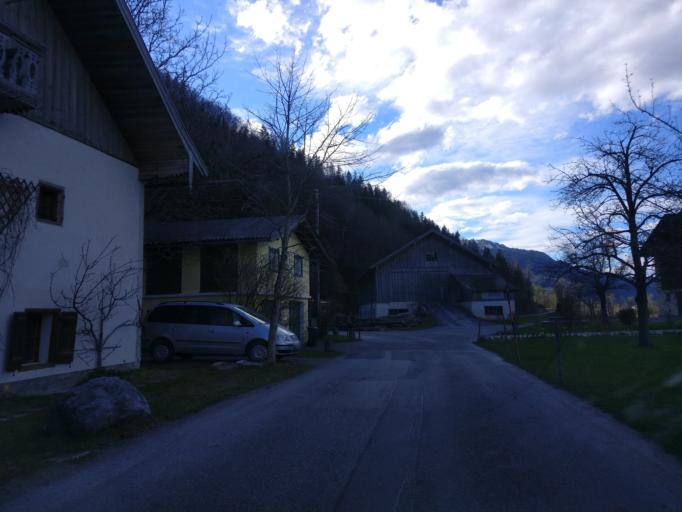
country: AT
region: Salzburg
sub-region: Politischer Bezirk Hallein
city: Golling an der Salzach
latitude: 47.5779
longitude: 13.1750
